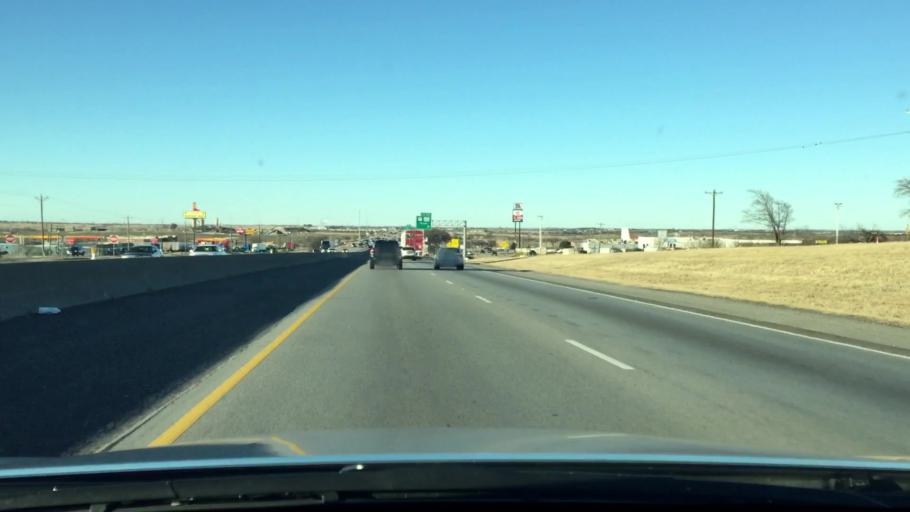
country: US
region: Texas
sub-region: Denton County
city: Krum
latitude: 33.2585
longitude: -97.1777
